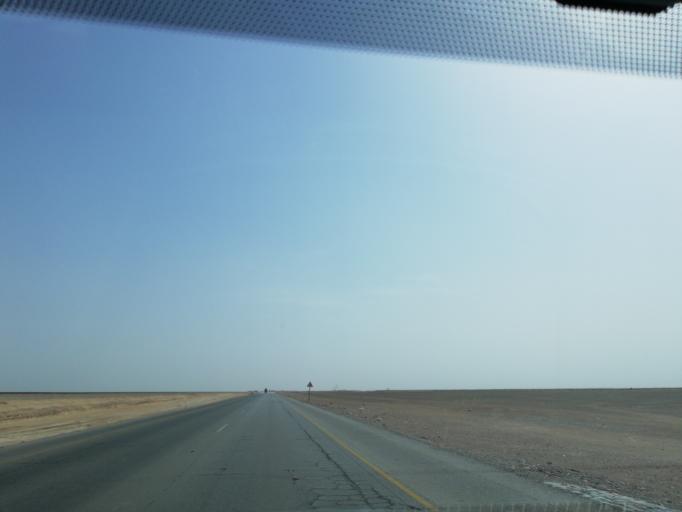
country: OM
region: Muhafazat ad Dakhiliyah
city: Adam
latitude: 21.6645
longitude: 57.3191
